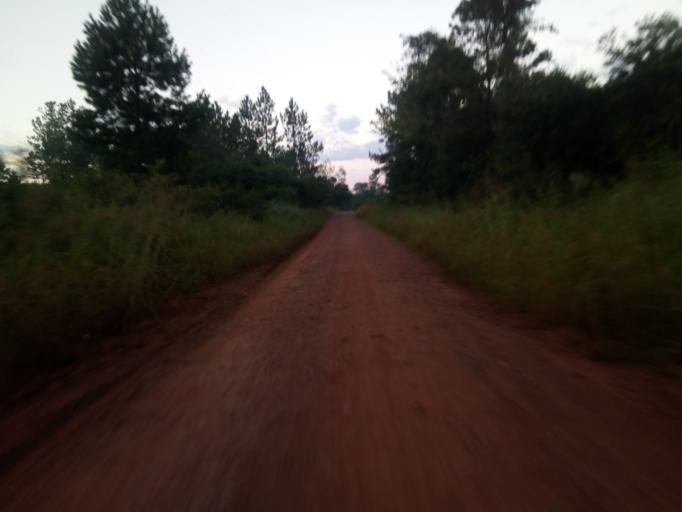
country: AR
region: Misiones
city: Almafuerte
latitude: -27.5637
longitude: -55.4096
